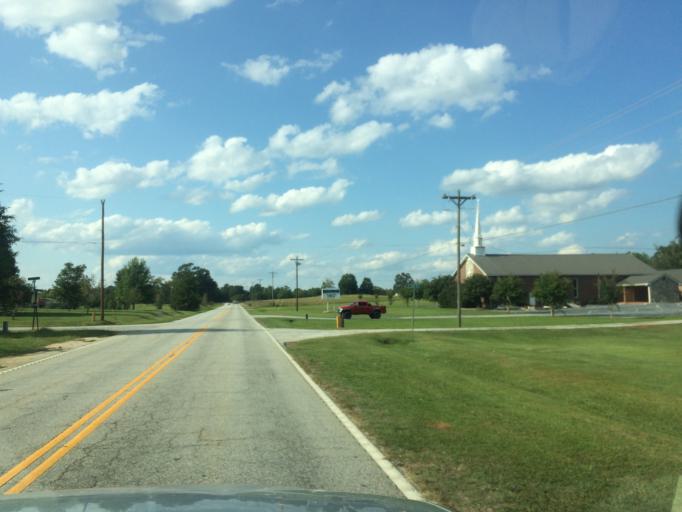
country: US
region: South Carolina
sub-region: Greenwood County
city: Ware Shoals
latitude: 34.5298
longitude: -82.1945
